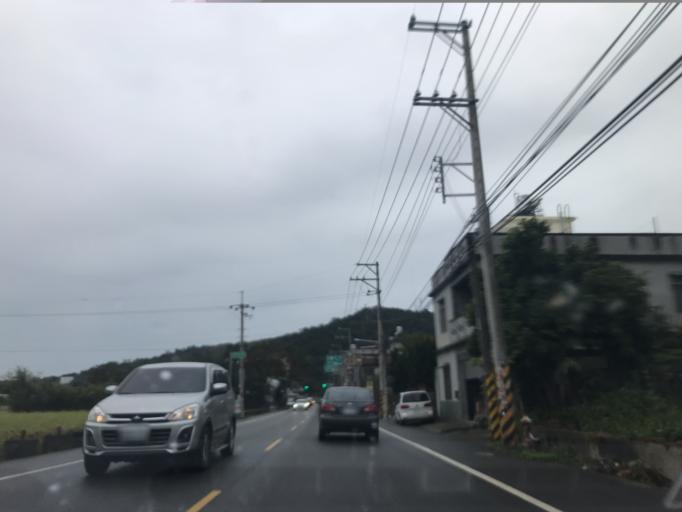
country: TW
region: Taiwan
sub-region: Hsinchu
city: Zhubei
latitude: 24.8391
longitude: 121.1025
